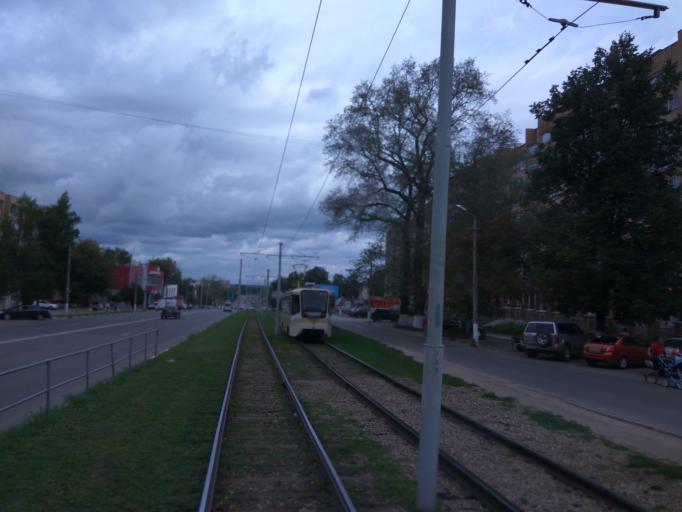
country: RU
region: Moskovskaya
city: Kolomna
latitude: 55.0848
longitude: 38.7642
